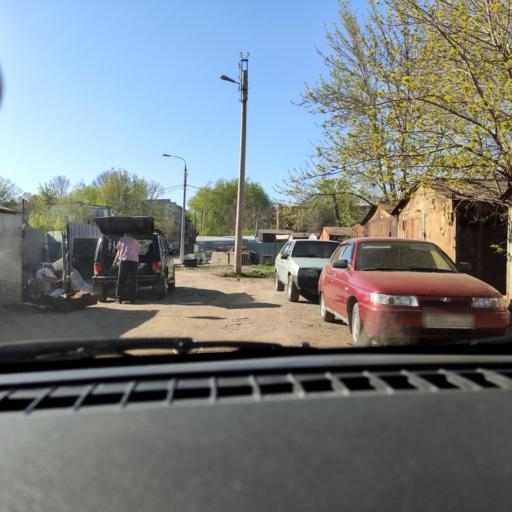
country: RU
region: Samara
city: Samara
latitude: 53.2065
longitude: 50.2492
